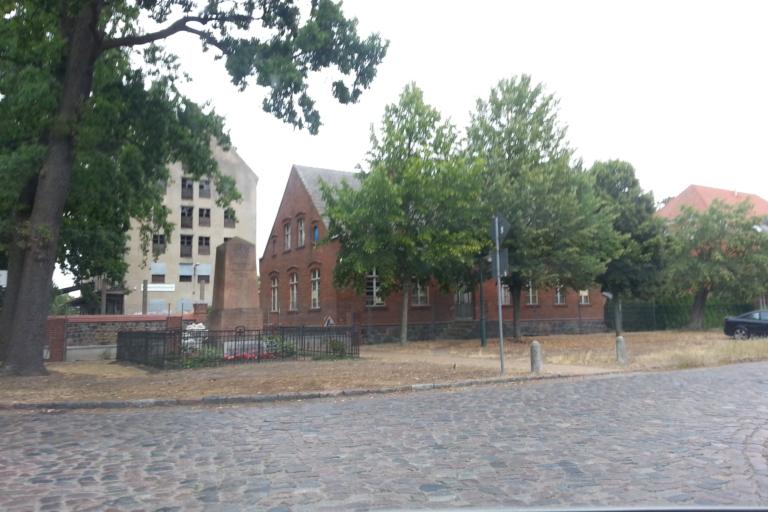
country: DE
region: Mecklenburg-Vorpommern
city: Ferdinandshof
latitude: 53.6640
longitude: 13.8859
